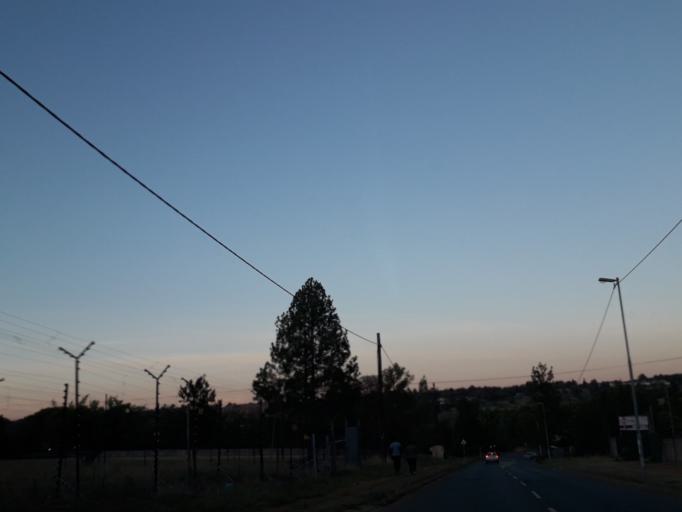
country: ZA
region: Gauteng
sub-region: West Rand District Municipality
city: Muldersdriseloop
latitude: -26.0872
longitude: 27.9000
